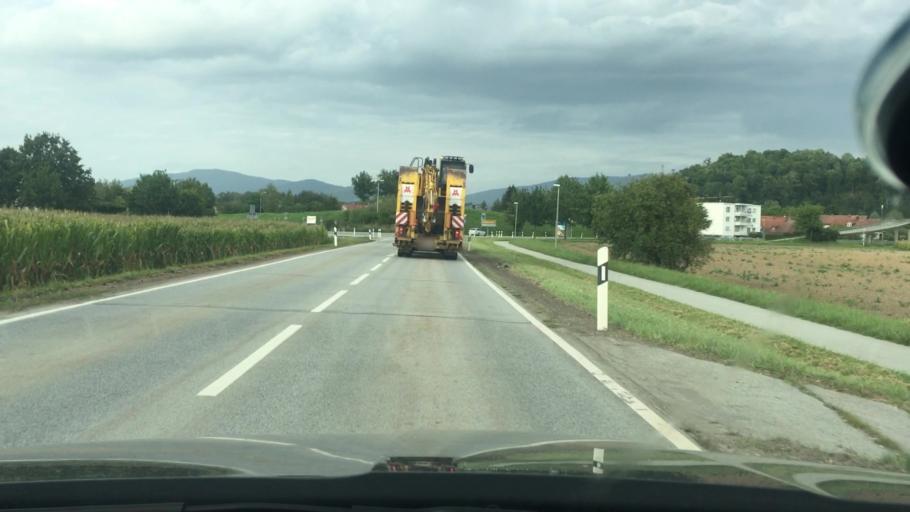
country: DE
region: Bavaria
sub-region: Lower Bavaria
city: Metten
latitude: 48.8201
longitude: 12.9019
